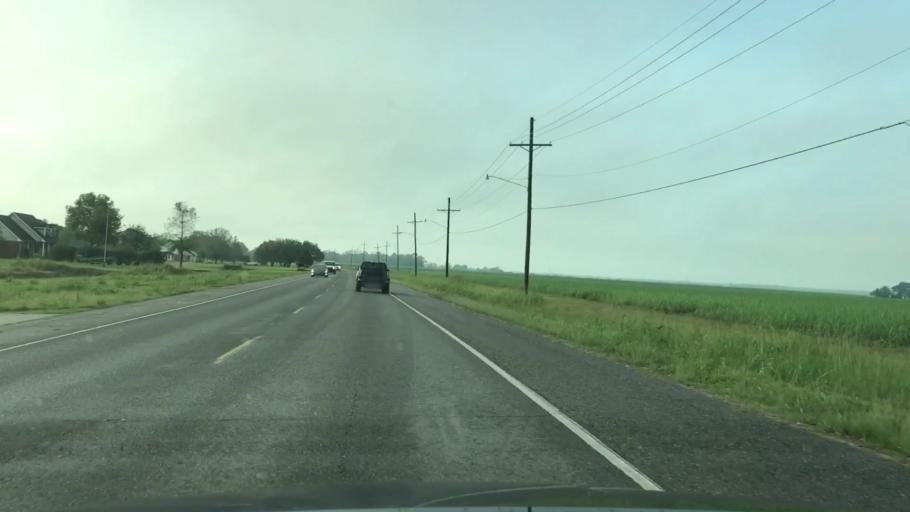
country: US
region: Louisiana
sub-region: Terrebonne Parish
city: Gray
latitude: 29.6619
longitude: -90.8204
